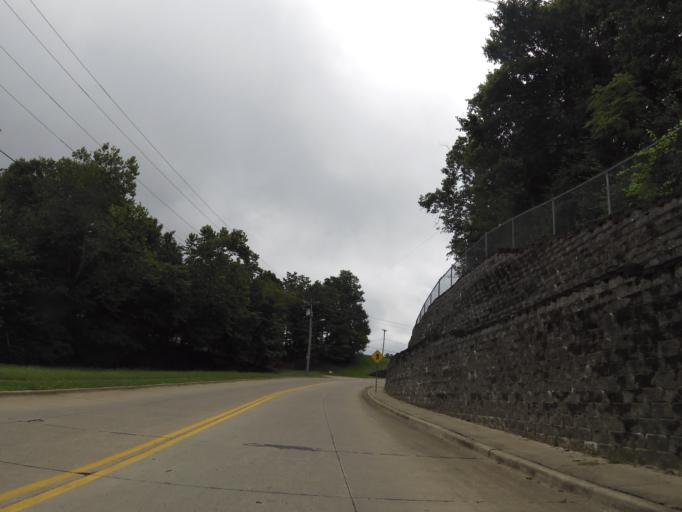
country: US
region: Missouri
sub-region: Cape Girardeau County
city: Cape Girardeau
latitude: 37.3494
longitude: -89.5599
